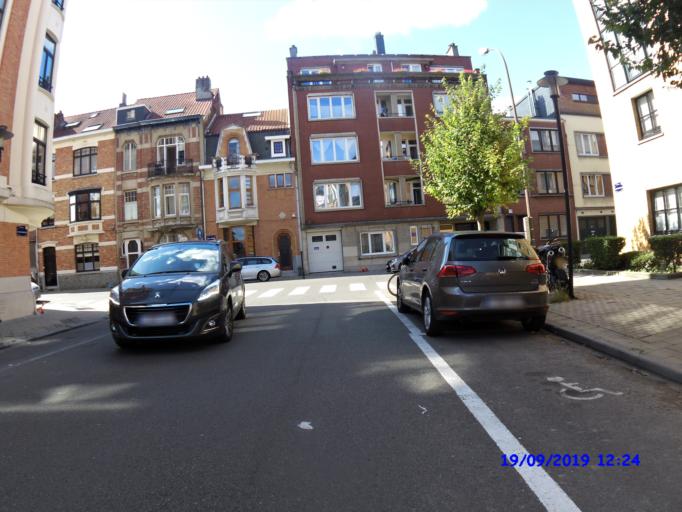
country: BE
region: Brussels Capital
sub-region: Bruxelles-Capitale
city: Brussels
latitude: 50.8247
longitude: 4.3814
